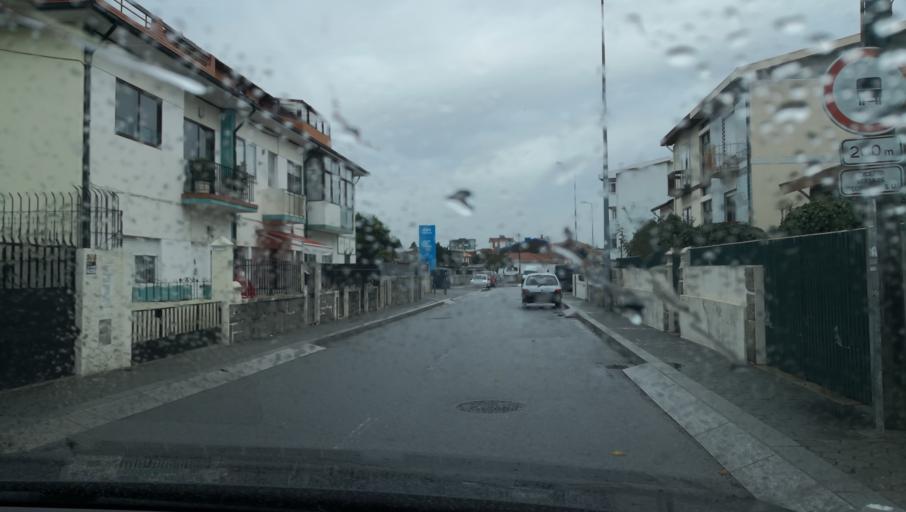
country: PT
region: Porto
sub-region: Vila Nova de Gaia
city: Vila Nova de Gaia
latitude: 41.1202
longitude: -8.6275
